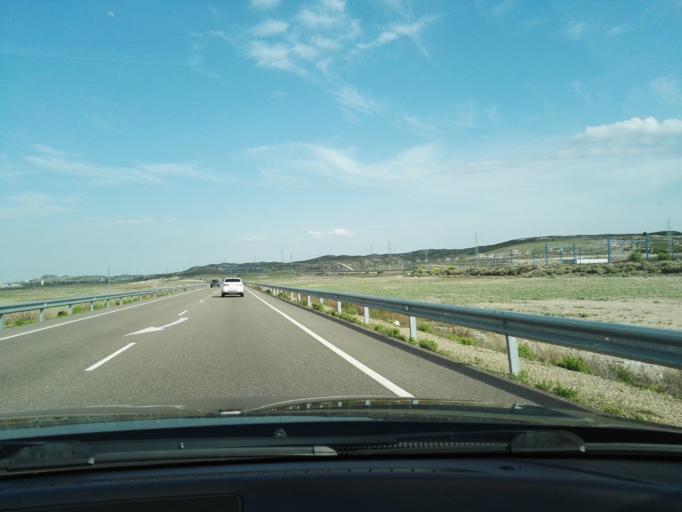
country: ES
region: Aragon
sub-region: Provincia de Zaragoza
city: Montecanal
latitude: 41.6248
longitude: -0.9863
